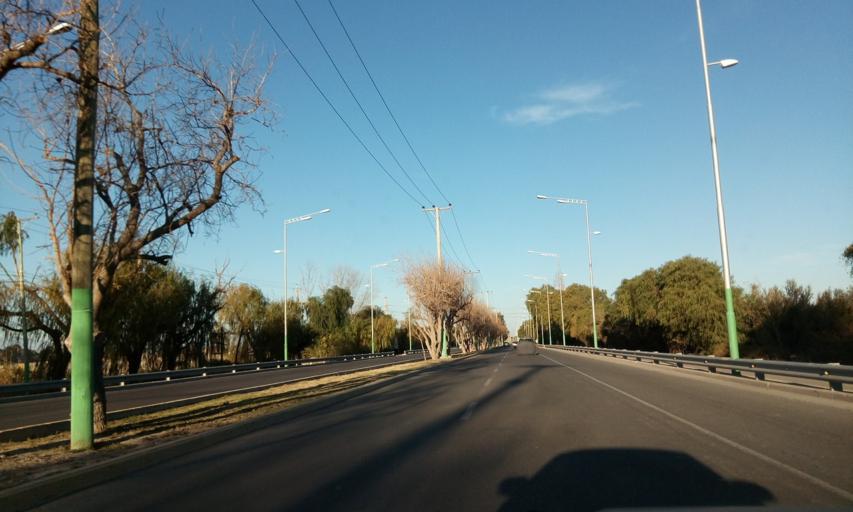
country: AR
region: San Juan
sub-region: Departamento de Rivadavia
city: Rivadavia
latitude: -31.5261
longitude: -68.6106
